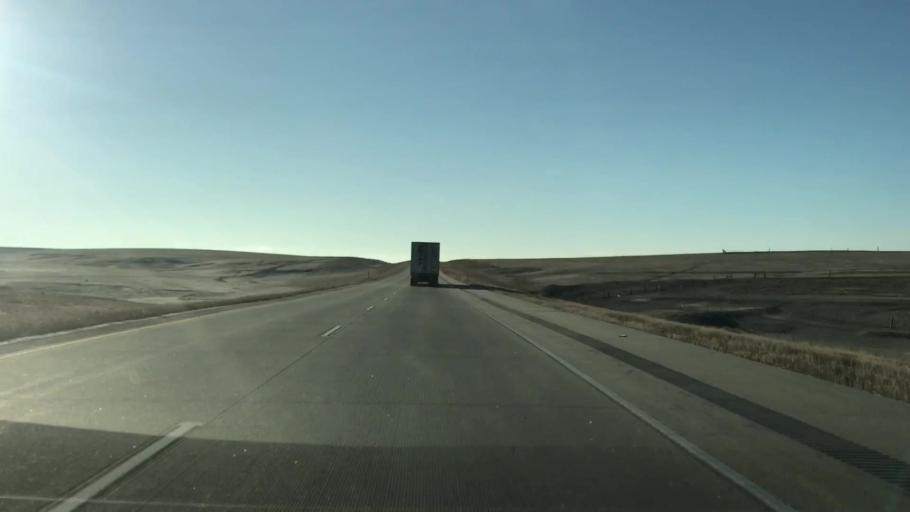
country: US
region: Colorado
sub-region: Lincoln County
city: Limon
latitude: 39.3991
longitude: -103.8990
